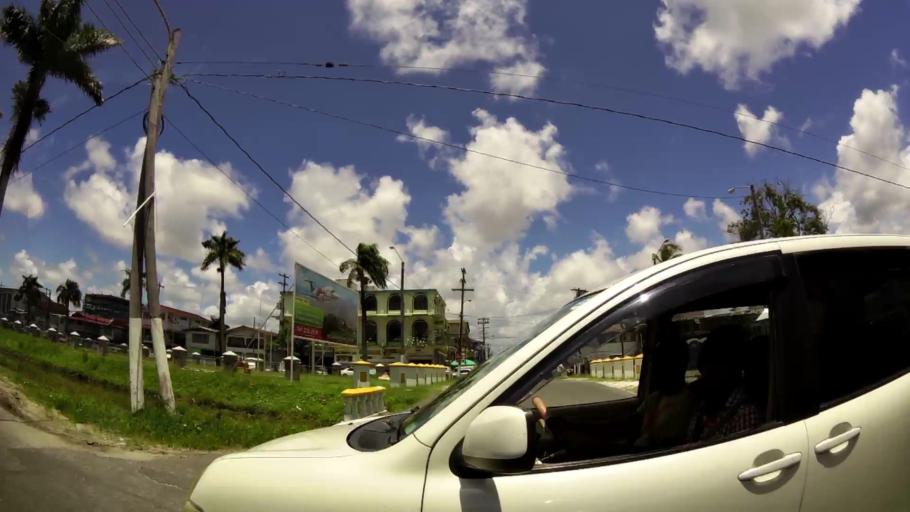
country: GY
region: Demerara-Mahaica
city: Georgetown
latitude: 6.8107
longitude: -58.1546
